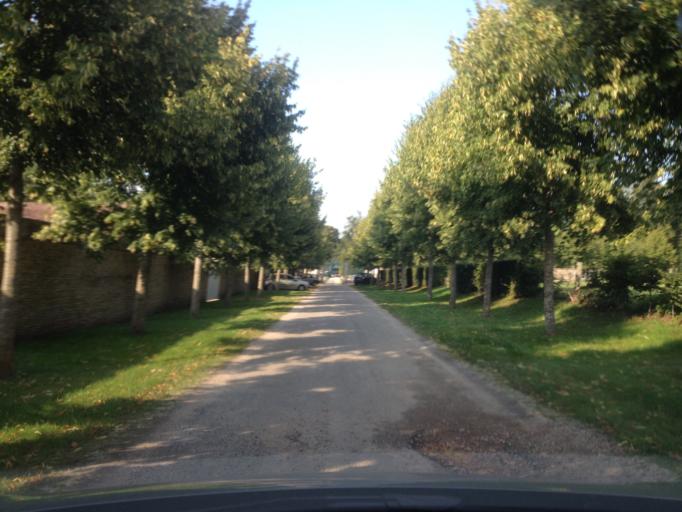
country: FR
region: Lower Normandy
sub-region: Departement du Calvados
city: Canon
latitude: 49.0767
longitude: -0.0950
